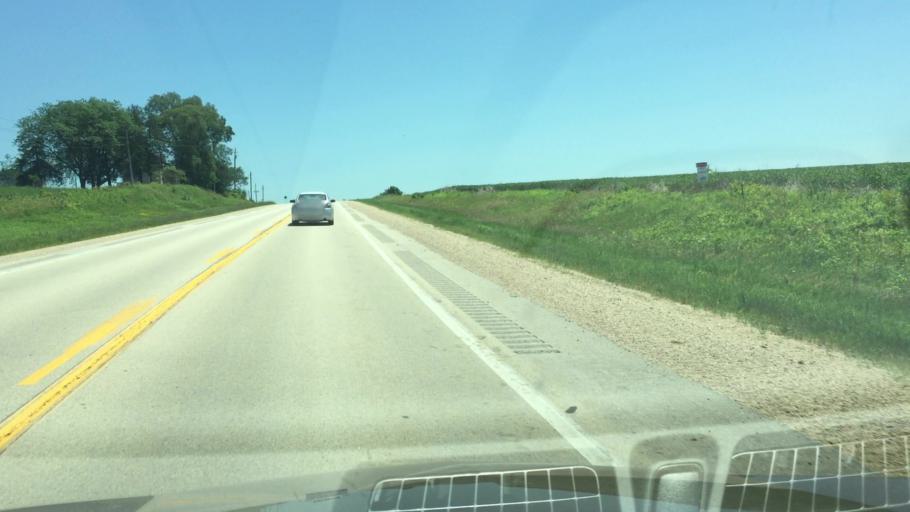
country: US
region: Iowa
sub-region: Jackson County
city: Maquoketa
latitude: 42.0720
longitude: -90.7983
